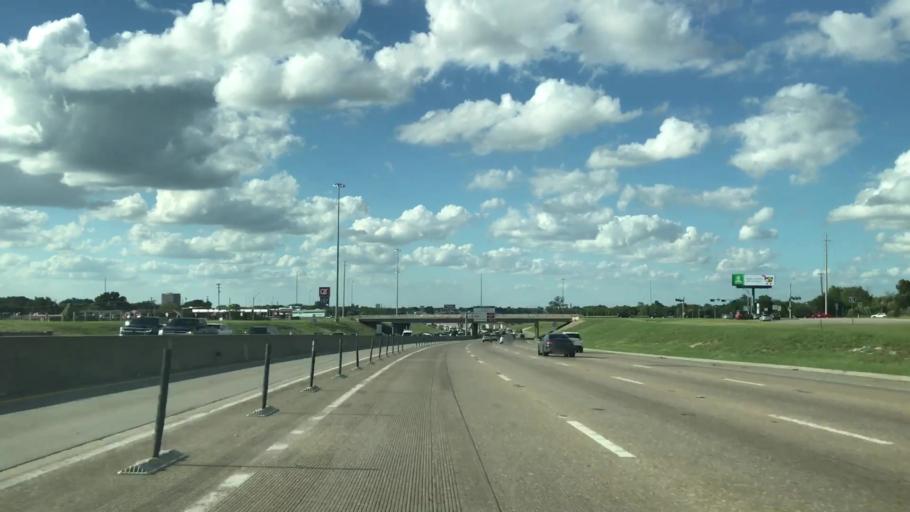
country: US
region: Texas
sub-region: Dallas County
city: Richardson
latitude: 32.8923
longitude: -96.7100
